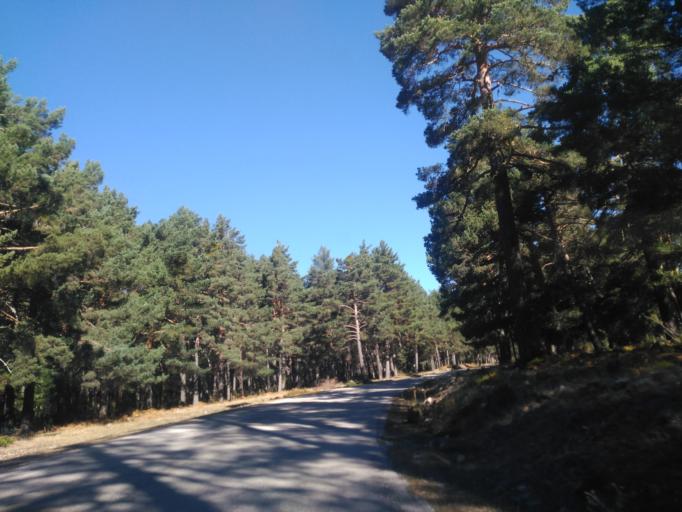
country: ES
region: Castille and Leon
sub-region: Provincia de Soria
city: Vinuesa
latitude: 41.9923
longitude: -2.8006
